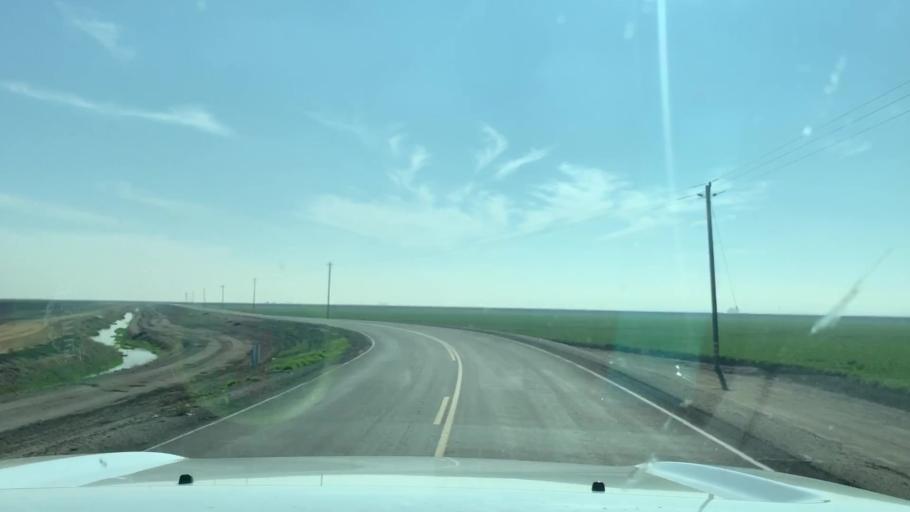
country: US
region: California
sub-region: Kern County
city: Buttonwillow
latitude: 35.4601
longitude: -119.5790
